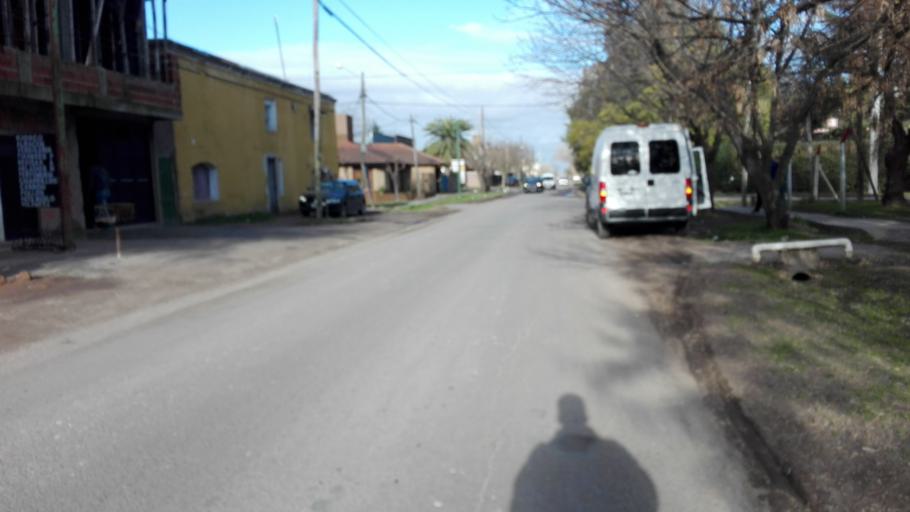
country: AR
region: Buenos Aires
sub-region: Partido de La Plata
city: La Plata
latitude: -34.9165
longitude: -58.0218
